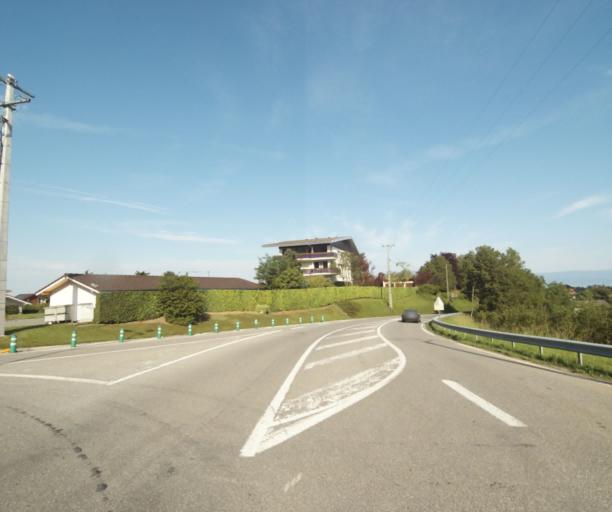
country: FR
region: Rhone-Alpes
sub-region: Departement de la Haute-Savoie
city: Armoy
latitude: 46.3464
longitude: 6.5238
